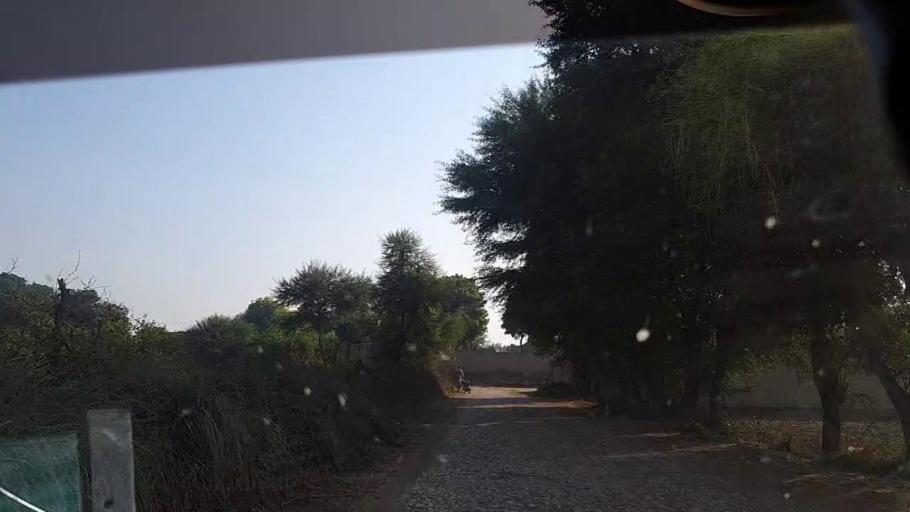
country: PK
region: Sindh
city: Hingorja
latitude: 27.2132
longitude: 68.2645
